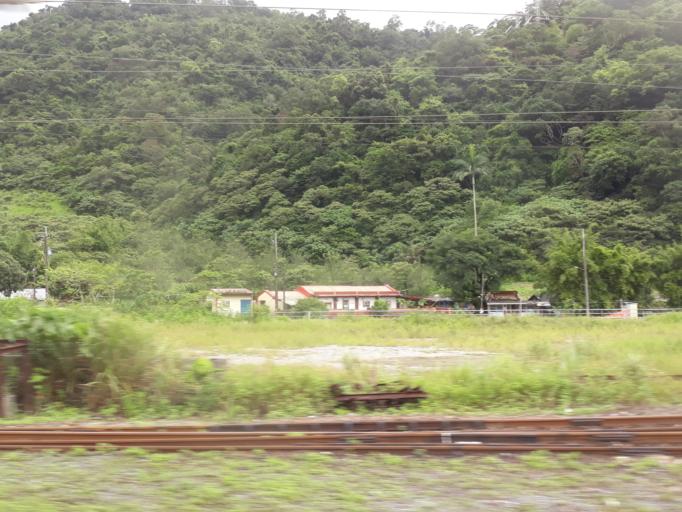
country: TW
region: Taiwan
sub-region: Yilan
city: Yilan
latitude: 24.5666
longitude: 121.8435
